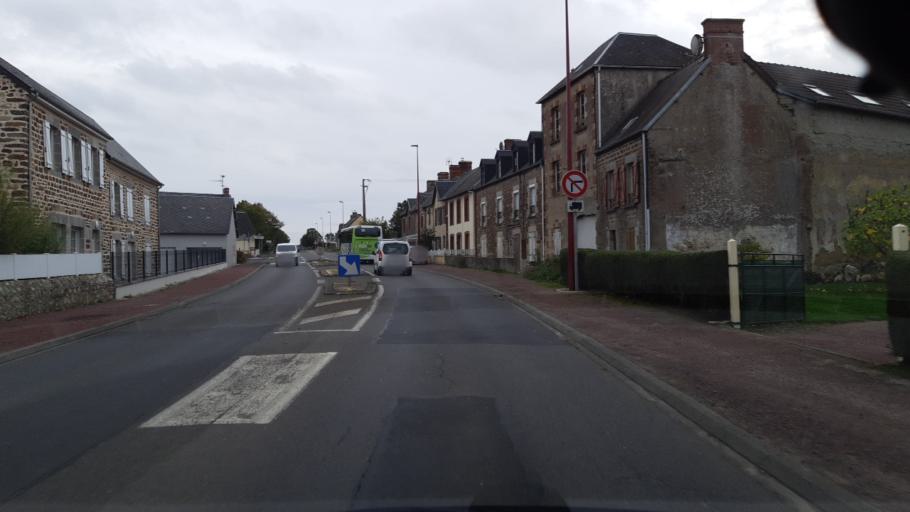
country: FR
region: Lower Normandy
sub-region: Departement de la Manche
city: Brehal
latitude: 48.8826
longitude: -1.5294
